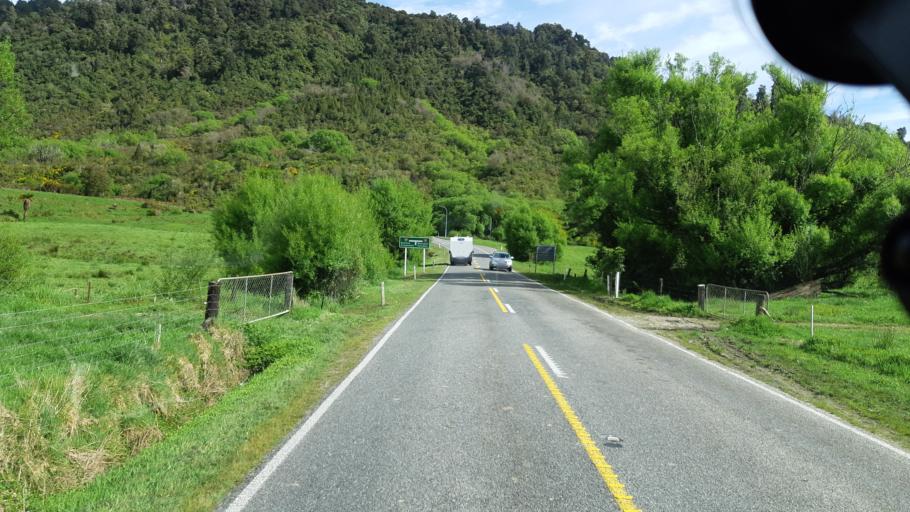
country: NZ
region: West Coast
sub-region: Buller District
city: Westport
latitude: -41.8593
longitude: 171.9389
